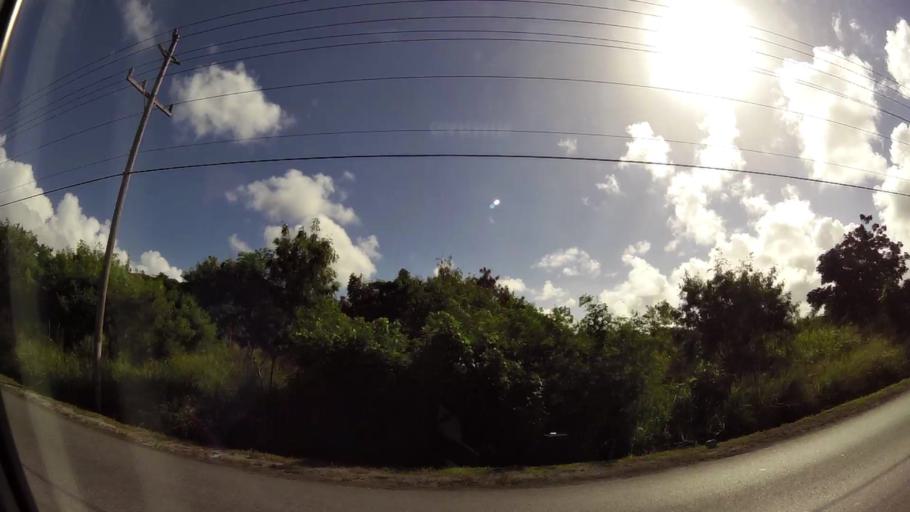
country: BB
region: Saint James
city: Holetown
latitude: 13.2046
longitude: -59.6177
